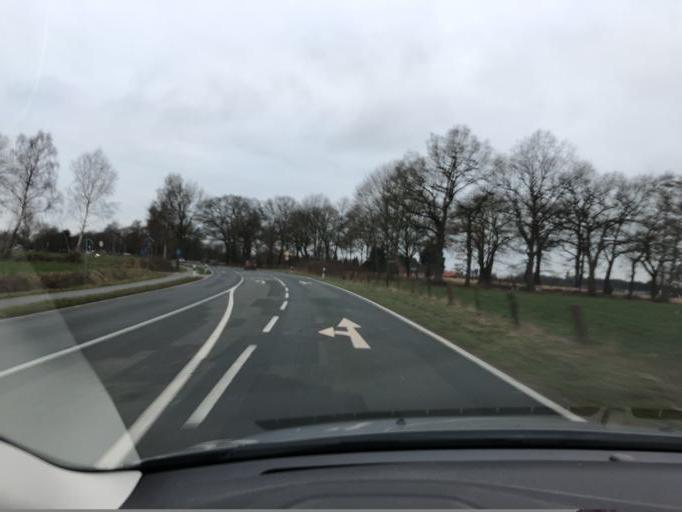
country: DE
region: Lower Saxony
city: Ganderkesee
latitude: 53.0531
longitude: 8.5591
